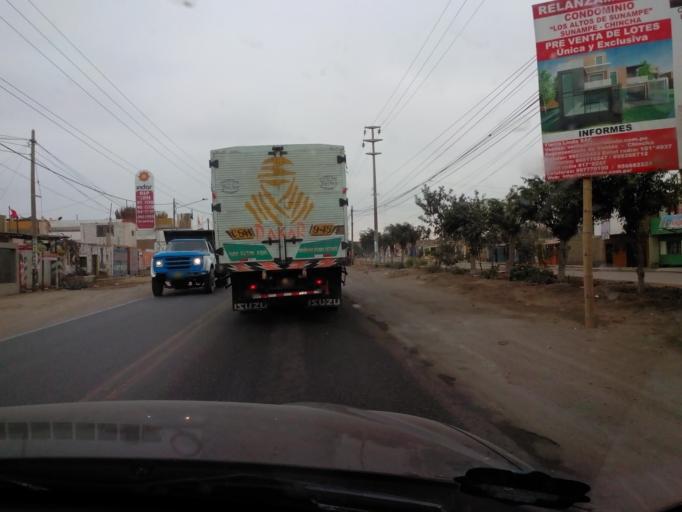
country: PE
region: Ica
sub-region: Provincia de Chincha
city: Chincha Alta
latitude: -13.4402
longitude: -76.1351
